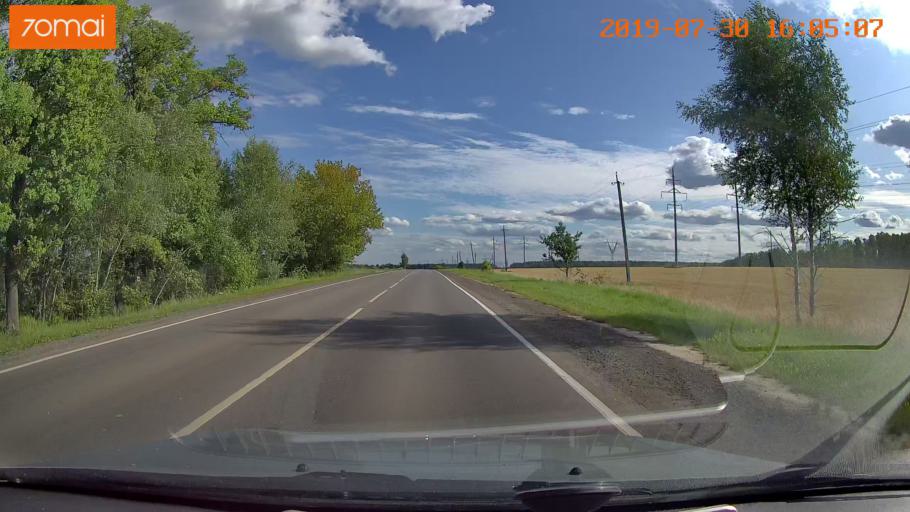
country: RU
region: Moskovskaya
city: Lopatinskiy
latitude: 55.2709
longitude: 38.7138
